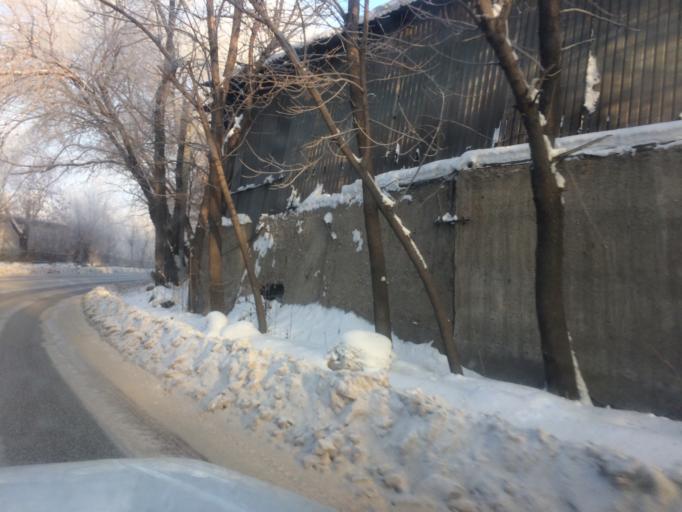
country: RU
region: Chelyabinsk
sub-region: Gorod Magnitogorsk
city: Magnitogorsk
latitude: 53.3937
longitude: 59.0712
